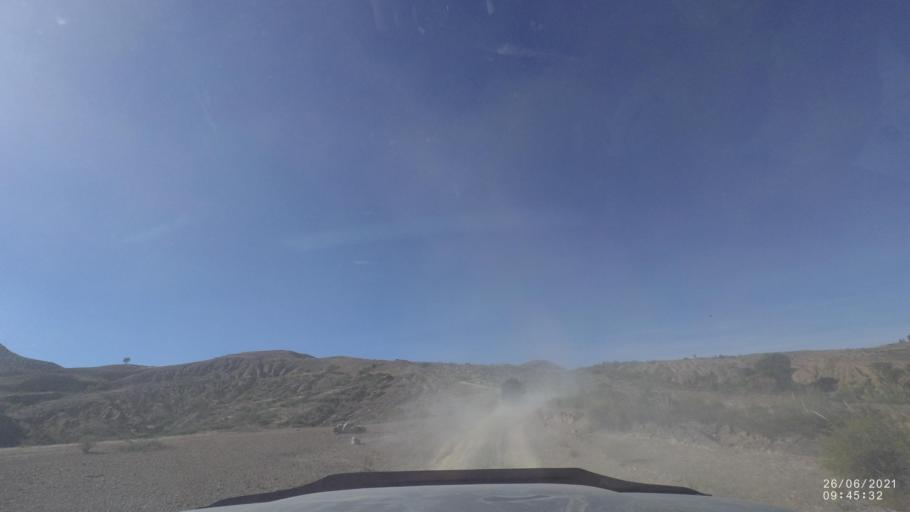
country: BO
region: Cochabamba
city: Mizque
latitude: -17.9479
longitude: -65.6298
